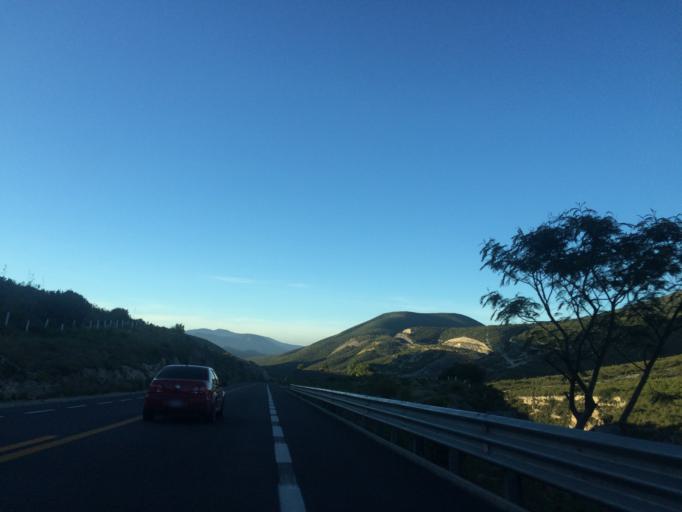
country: MX
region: Puebla
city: Chapuco
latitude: 18.6708
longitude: -97.4584
